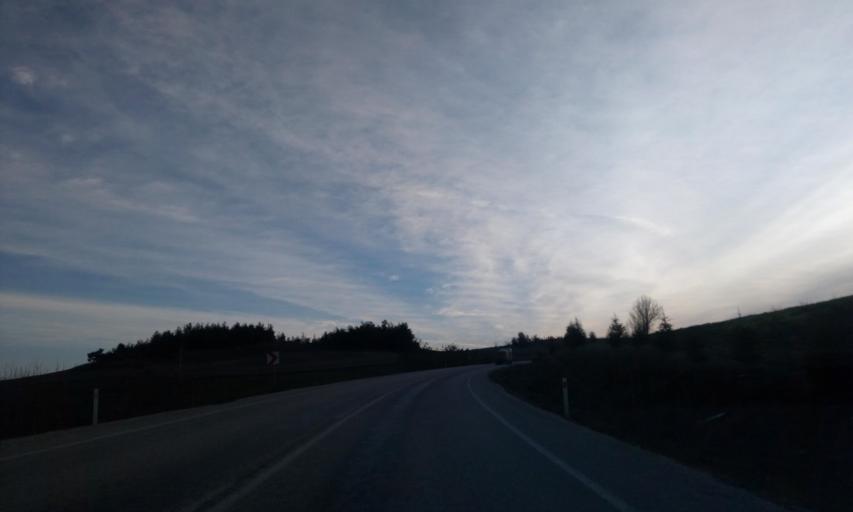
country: TR
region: Bilecik
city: Kuplu
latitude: 40.1116
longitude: 30.0733
